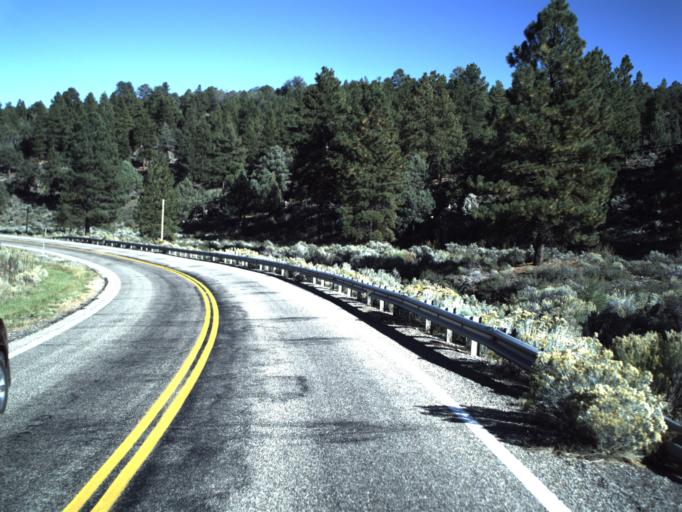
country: US
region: Utah
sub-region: Garfield County
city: Panguitch
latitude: 37.7664
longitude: -112.4607
